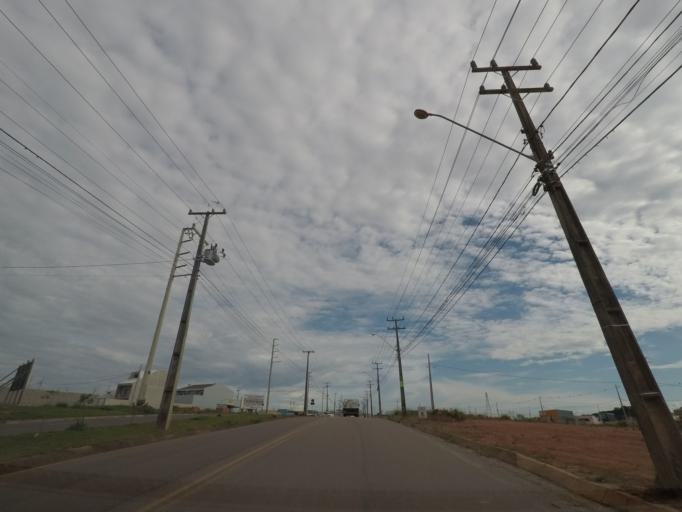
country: BR
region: Parana
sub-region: Araucaria
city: Araucaria
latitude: -25.6328
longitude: -49.2916
